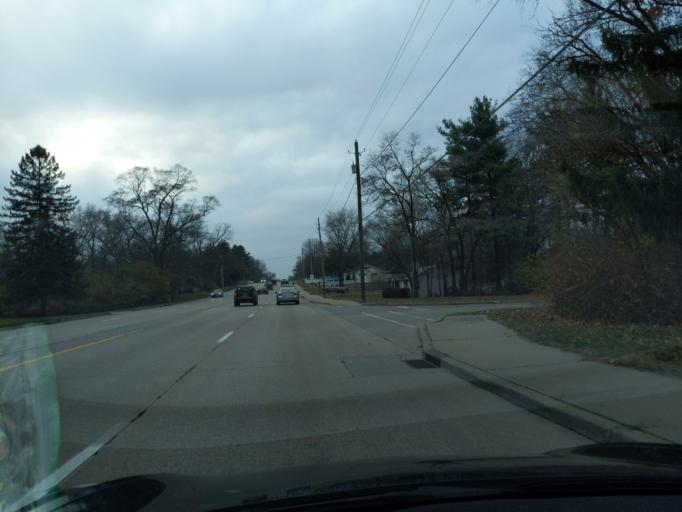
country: US
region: Indiana
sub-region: Saint Joseph County
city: Georgetown
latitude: 41.7232
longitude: -86.2404
